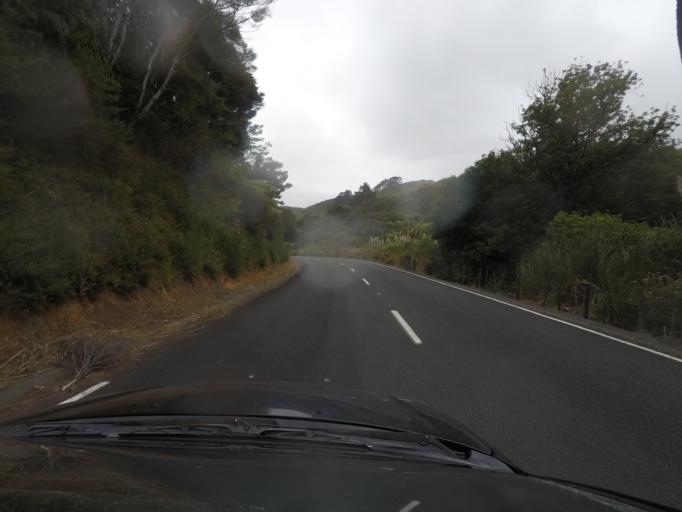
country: NZ
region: Auckland
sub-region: Auckland
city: Warkworth
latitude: -36.2798
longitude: 174.6946
